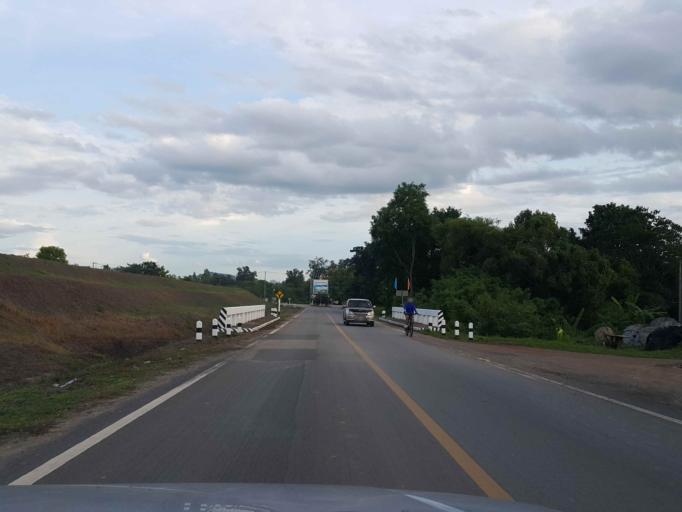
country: TH
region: Chiang Mai
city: San Sai
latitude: 18.8867
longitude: 99.1541
